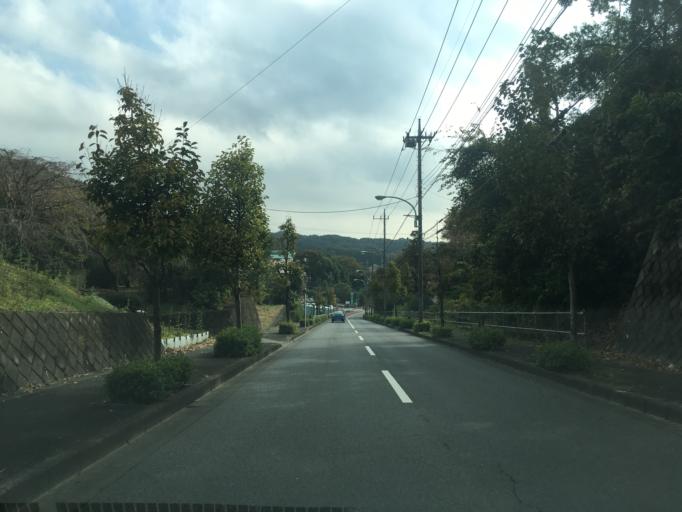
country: JP
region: Tokyo
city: Hino
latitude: 35.6063
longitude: 139.4200
